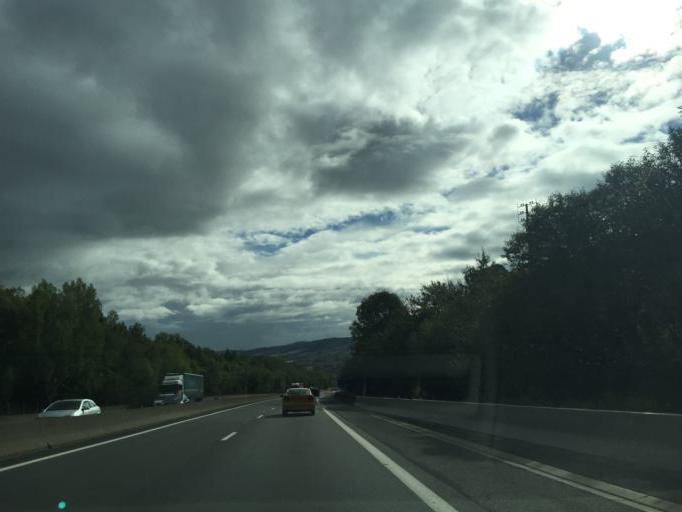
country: FR
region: Rhone-Alpes
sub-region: Departement de la Loire
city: La Grand-Croix
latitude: 45.4943
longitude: 4.5401
